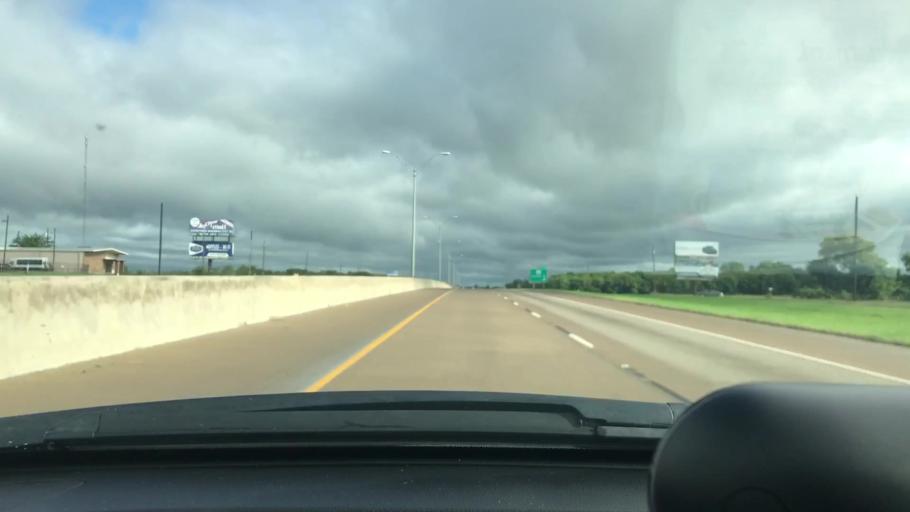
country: US
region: Texas
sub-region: Grayson County
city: Howe
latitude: 33.4857
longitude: -96.6200
